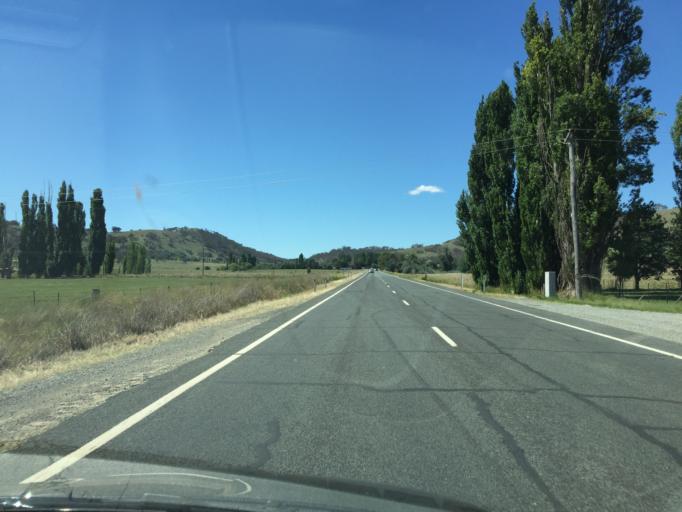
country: AU
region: Australian Capital Territory
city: Macarthur
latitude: -35.6942
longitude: 149.1629
